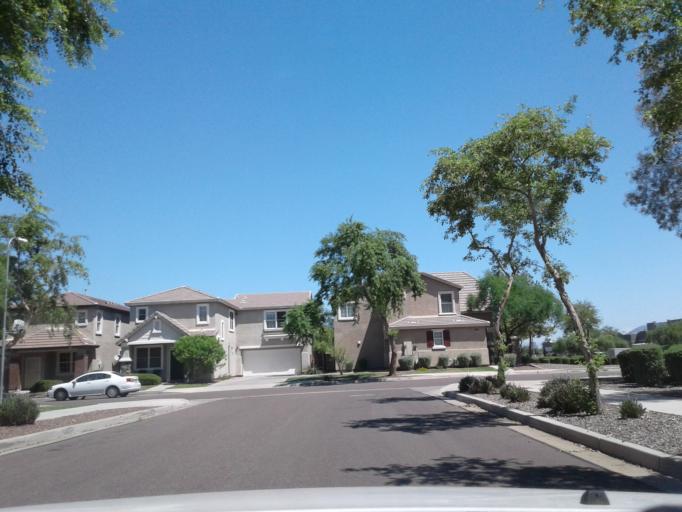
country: US
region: Arizona
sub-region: Maricopa County
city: Phoenix
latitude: 33.3946
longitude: -112.0305
